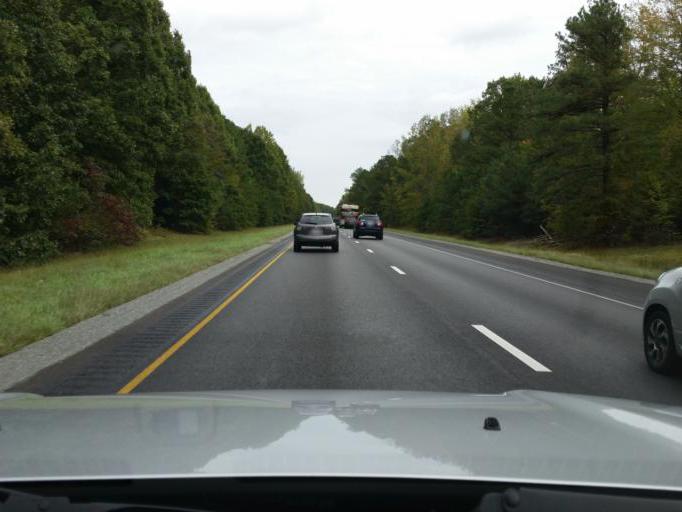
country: US
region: Virginia
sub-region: New Kent County
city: New Kent
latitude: 37.4893
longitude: -76.9782
